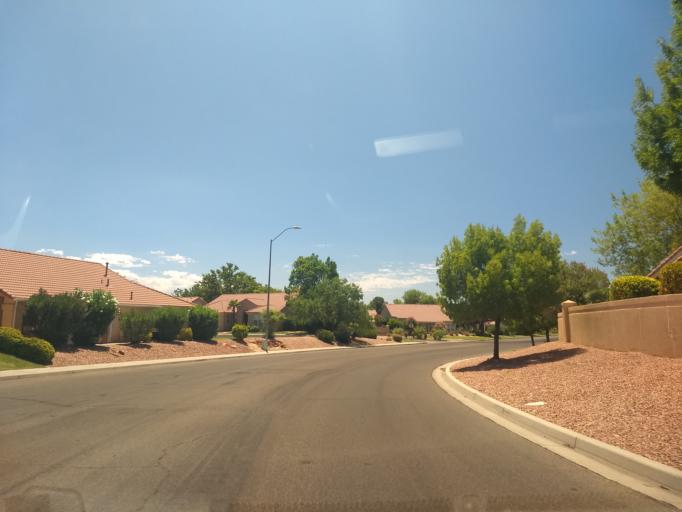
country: US
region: Utah
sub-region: Washington County
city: Washington
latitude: 37.1408
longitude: -113.5238
